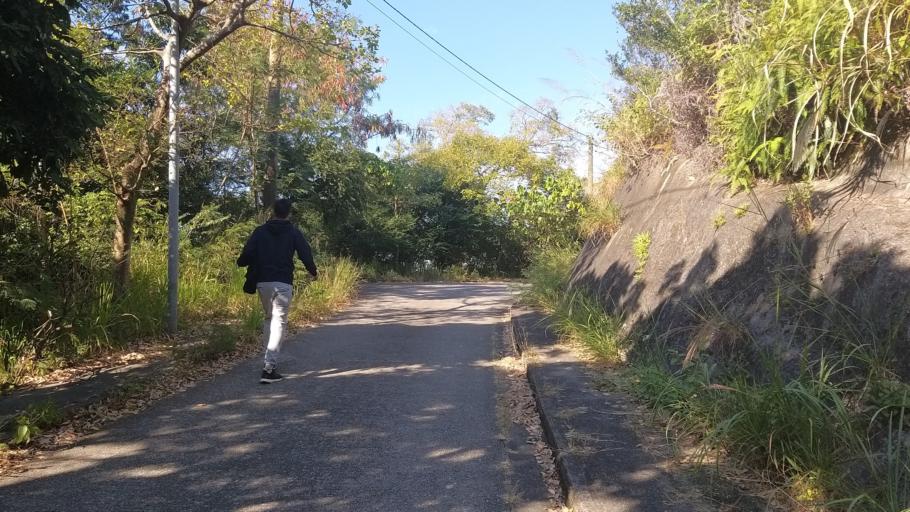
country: HK
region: Tuen Mun
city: Tuen Mun
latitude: 22.4052
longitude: 113.9866
